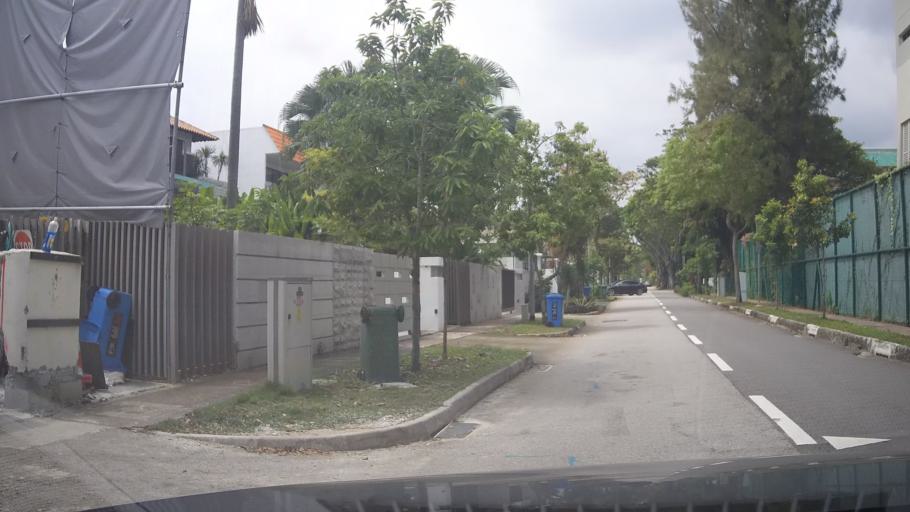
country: SG
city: Singapore
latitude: 1.3045
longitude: 103.8922
